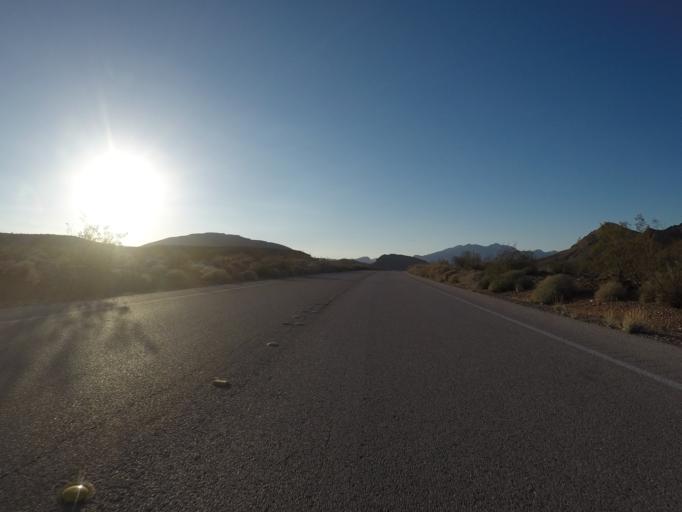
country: US
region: Nevada
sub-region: Clark County
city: Moapa Valley
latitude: 36.2417
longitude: -114.5278
